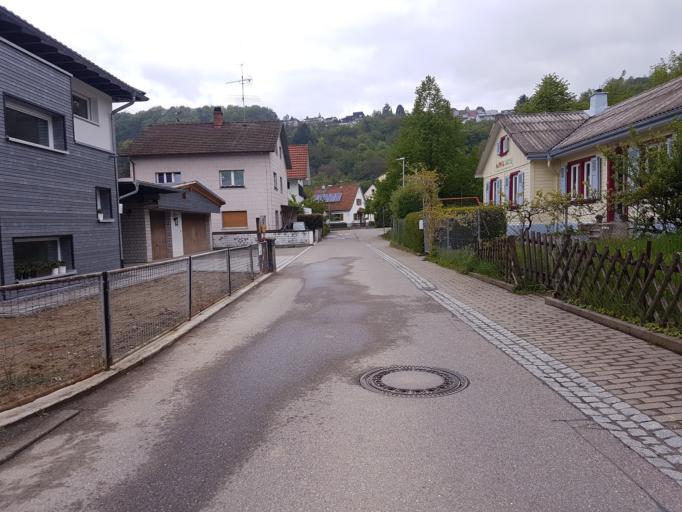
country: DE
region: Baden-Wuerttemberg
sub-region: Freiburg Region
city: Lauchringen
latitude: 47.6357
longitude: 8.2894
